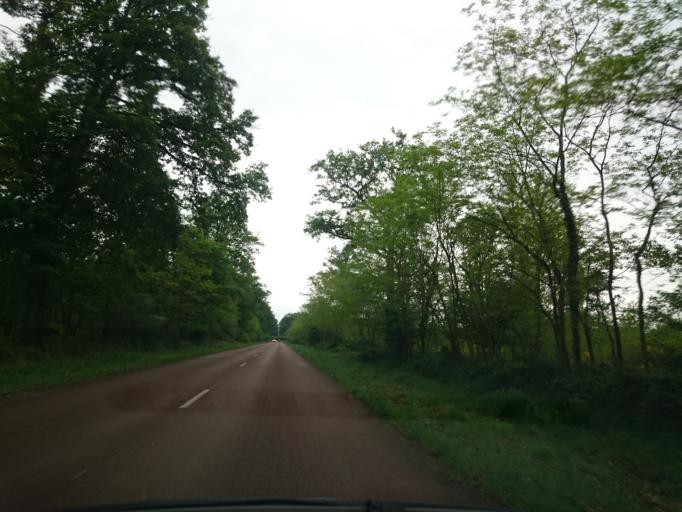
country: FR
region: Centre
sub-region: Departement du Loir-et-Cher
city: Muides-sur-Loire
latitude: 47.6409
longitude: 1.5225
